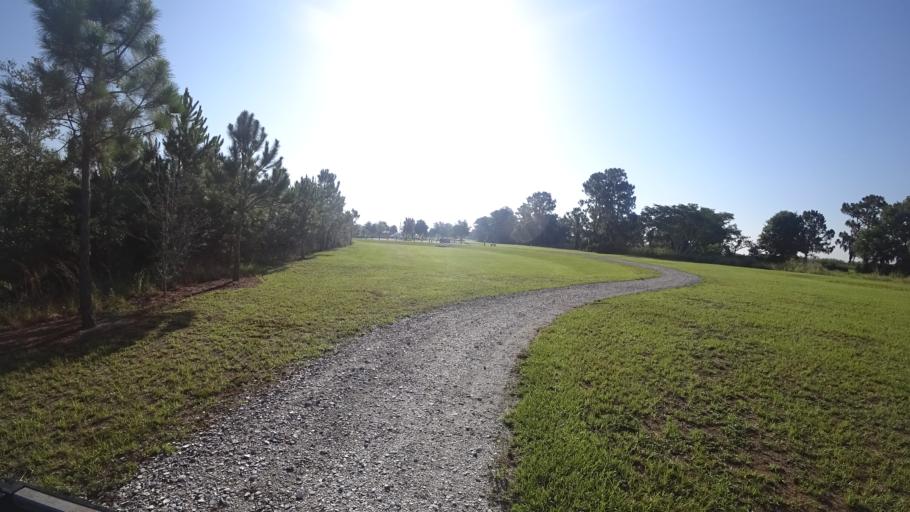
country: US
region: Florida
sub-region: Hillsborough County
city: Wimauma
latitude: 27.5841
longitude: -82.1785
